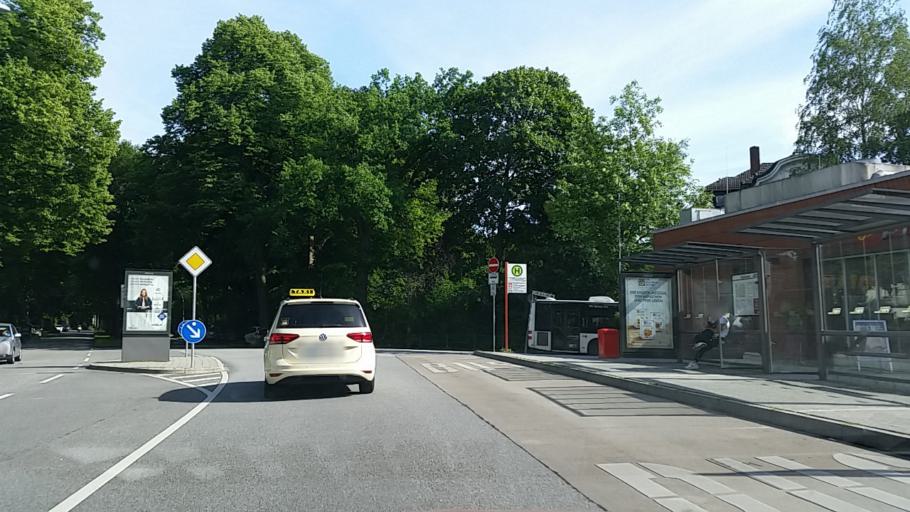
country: DE
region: Hamburg
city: Altona
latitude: 53.5589
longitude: 9.8872
